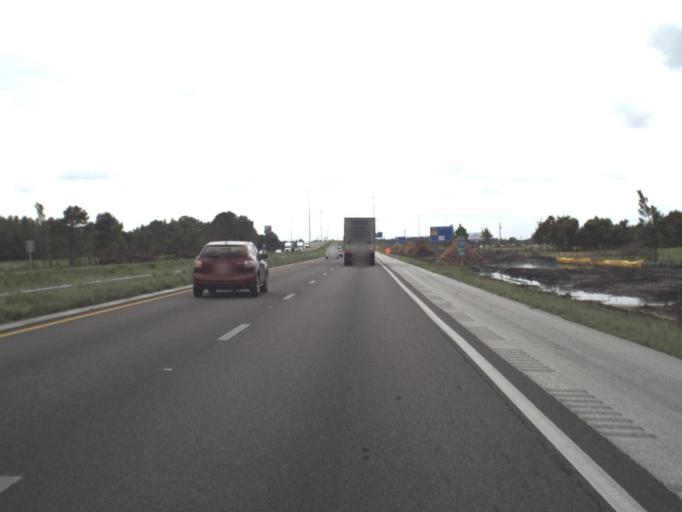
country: US
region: Florida
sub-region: Pasco County
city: San Antonio
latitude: 28.3354
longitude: -82.3240
